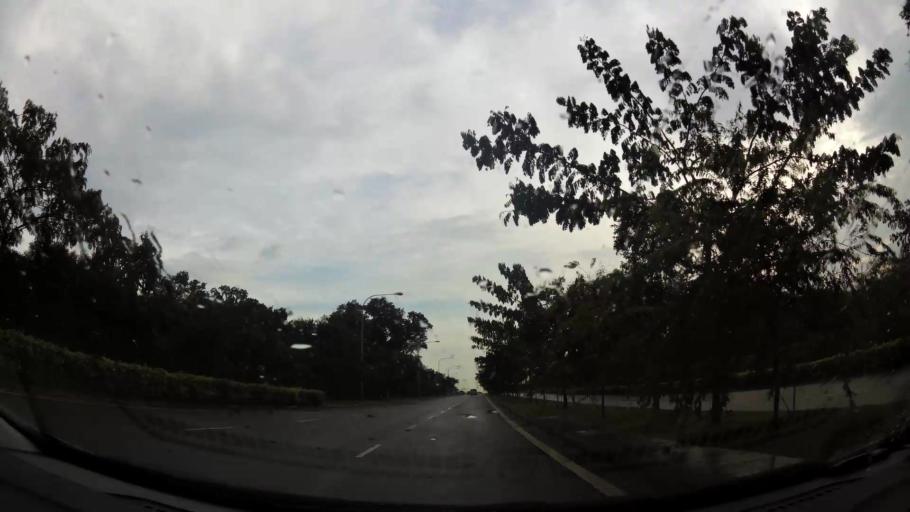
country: MY
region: Johor
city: Kampung Pasir Gudang Baru
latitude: 1.4043
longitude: 103.8689
